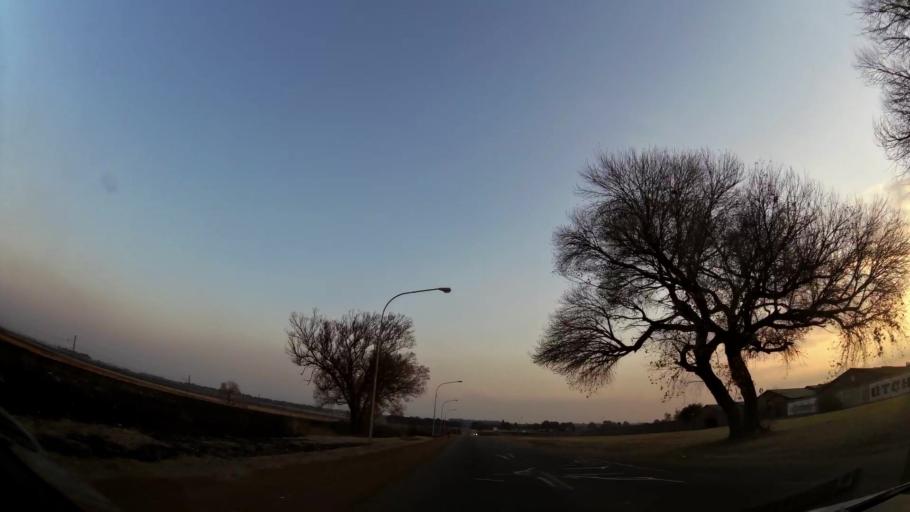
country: ZA
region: Gauteng
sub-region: Ekurhuleni Metropolitan Municipality
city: Springs
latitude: -26.3281
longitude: 28.4446
